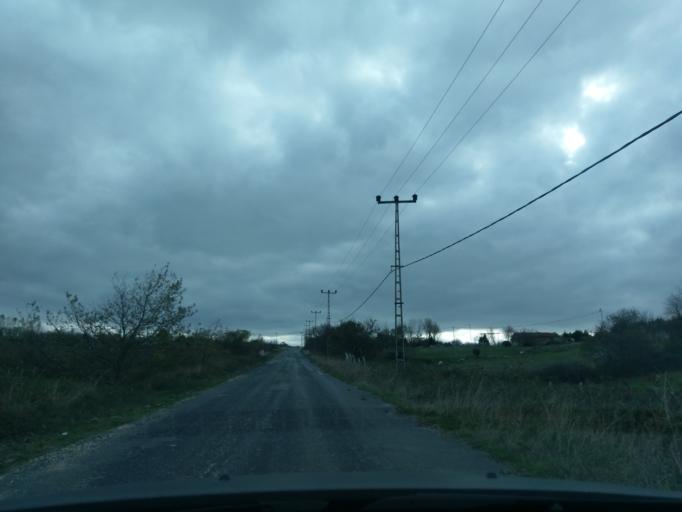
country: TR
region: Istanbul
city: Durusu
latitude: 41.2882
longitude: 28.6892
